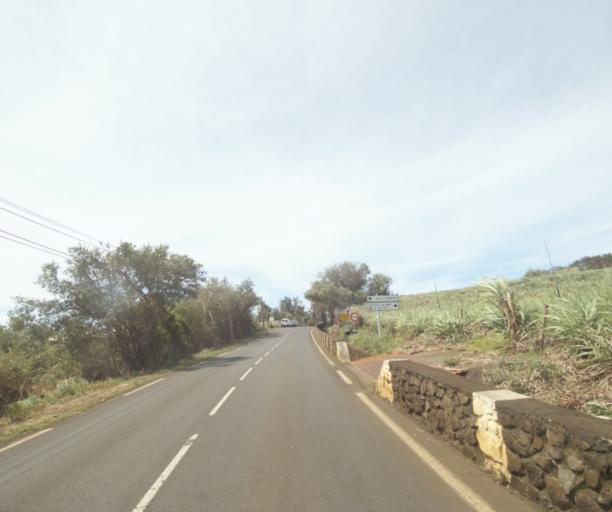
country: RE
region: Reunion
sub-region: Reunion
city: Saint-Paul
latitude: -21.0394
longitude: 55.2880
